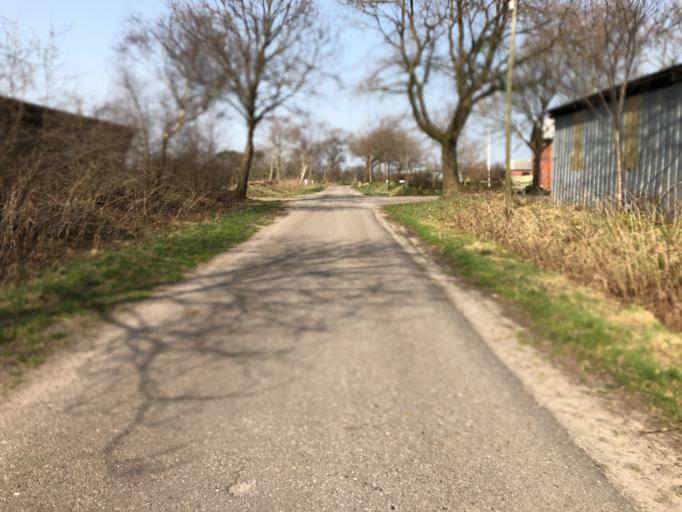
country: DE
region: Schleswig-Holstein
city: Wanderup
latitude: 54.6772
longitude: 9.3365
